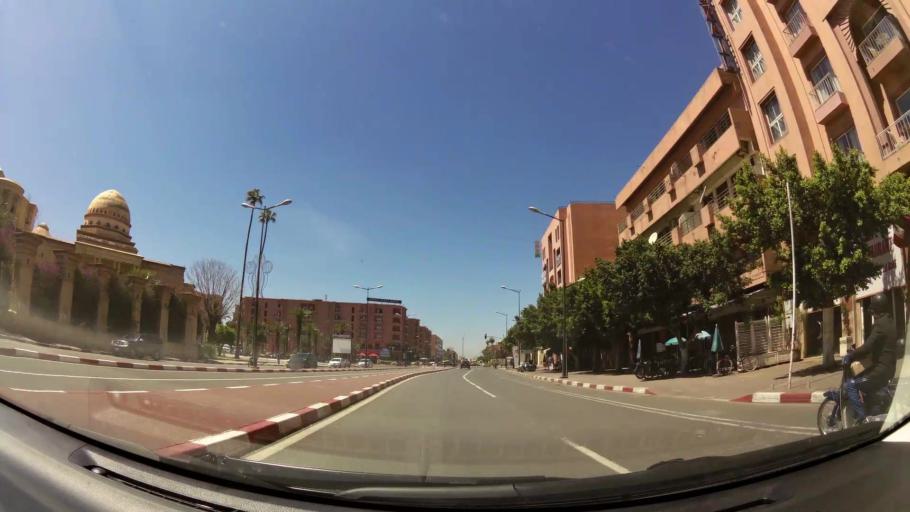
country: MA
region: Marrakech-Tensift-Al Haouz
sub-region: Marrakech
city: Marrakesh
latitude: 31.6305
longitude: -8.0149
